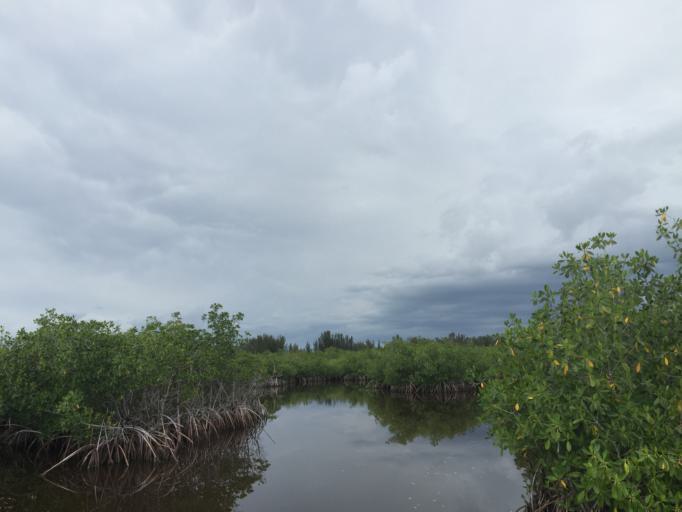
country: US
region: Florida
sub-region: Collier County
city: Marco
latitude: 25.9108
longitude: -81.3700
